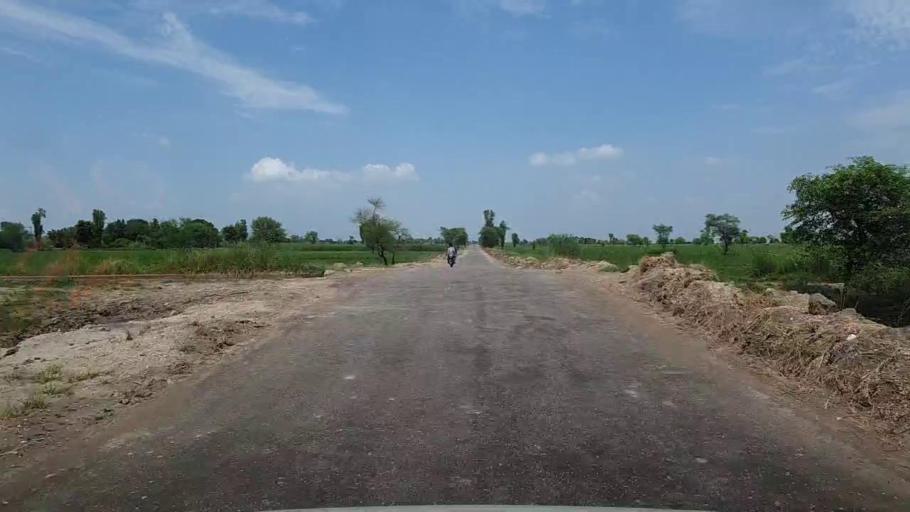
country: PK
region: Sindh
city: Bhiria
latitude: 26.9255
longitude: 68.2094
